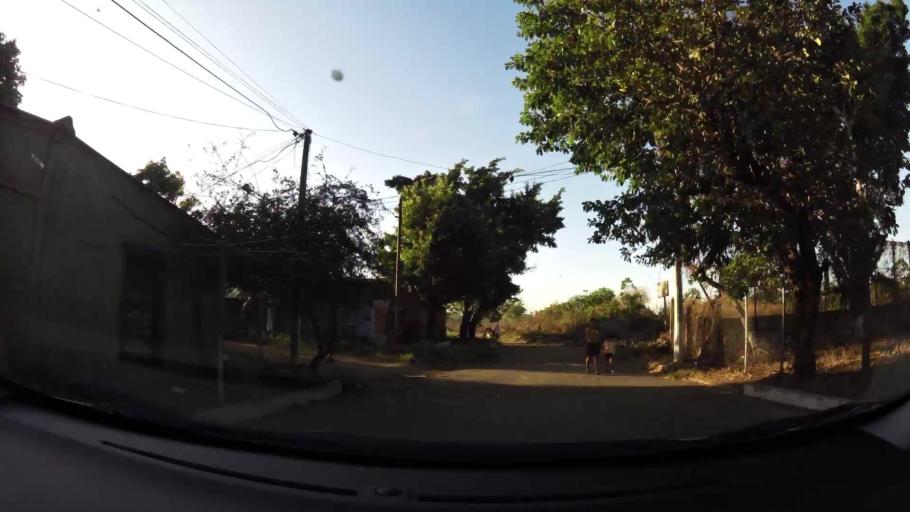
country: SV
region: Sonsonate
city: San Antonio del Monte
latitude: 13.7057
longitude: -89.7341
